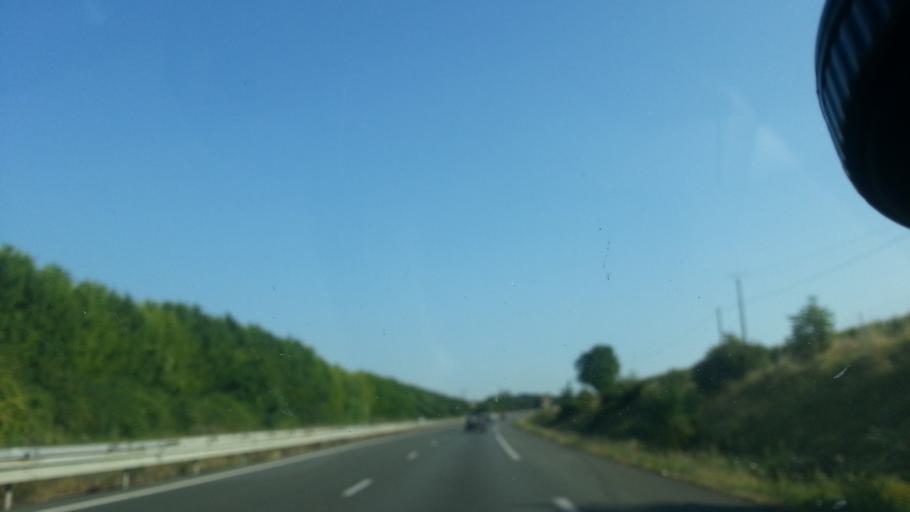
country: FR
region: Poitou-Charentes
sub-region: Departement de la Vienne
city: Antran
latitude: 46.8802
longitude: 0.5181
